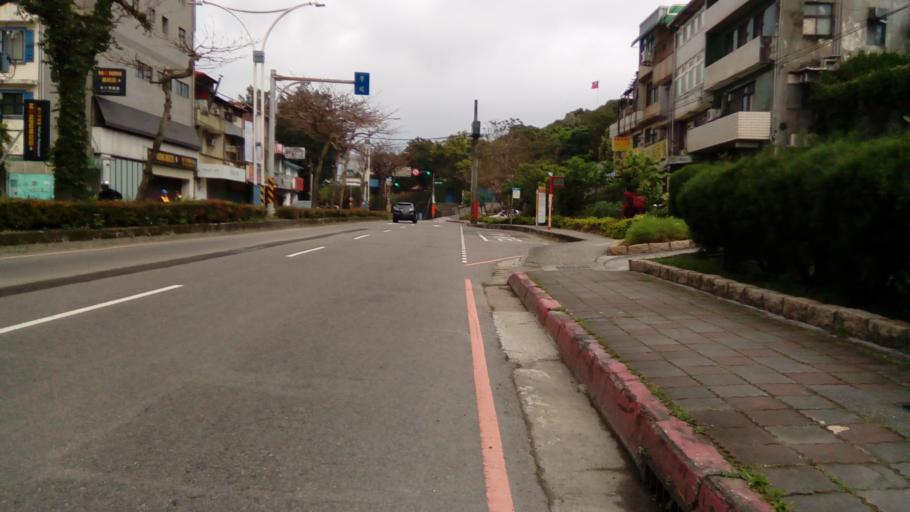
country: TW
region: Taipei
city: Taipei
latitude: 25.1740
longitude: 121.4347
